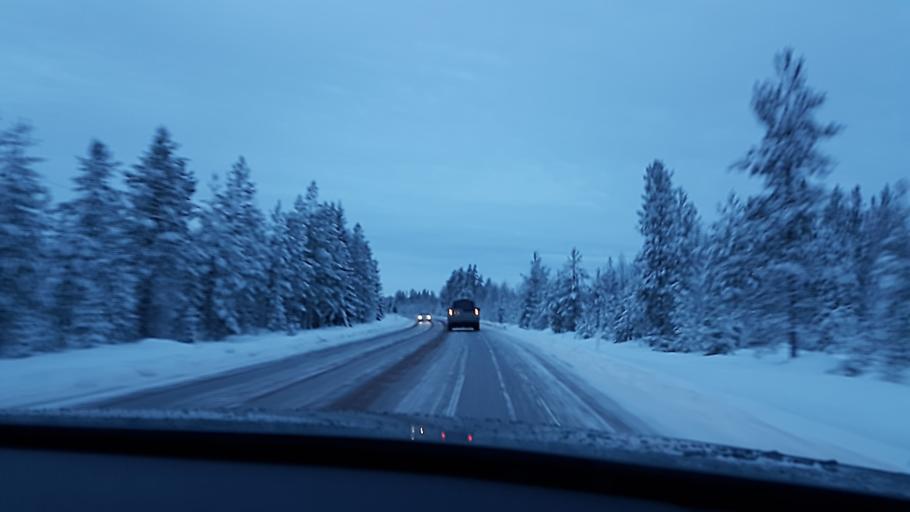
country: SE
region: Jaemtland
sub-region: Harjedalens Kommun
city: Sveg
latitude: 62.0550
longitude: 14.5456
